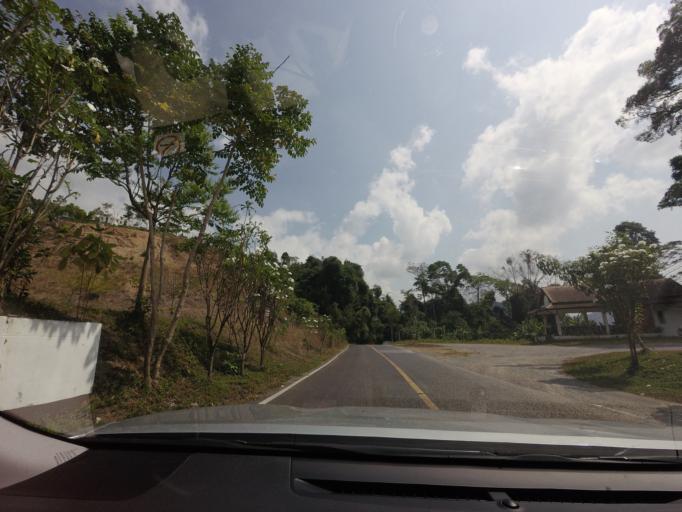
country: TH
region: Phangnga
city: Thap Put
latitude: 8.5355
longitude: 98.5587
